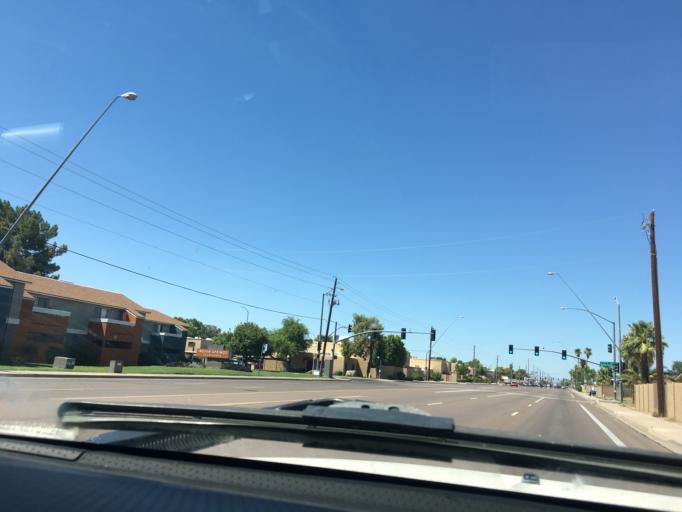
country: US
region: Arizona
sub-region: Maricopa County
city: Mesa
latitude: 33.3959
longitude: -111.8571
